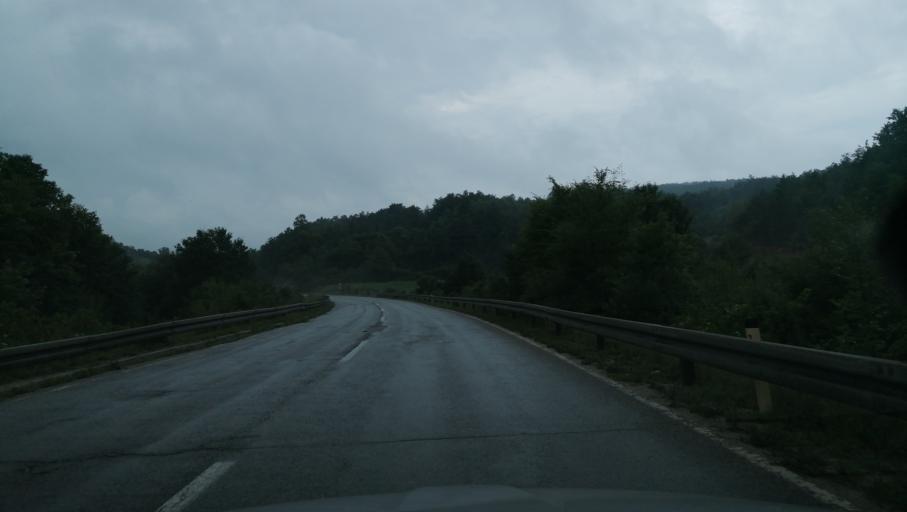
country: RS
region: Central Serbia
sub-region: Zlatiborski Okrug
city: Cajetina
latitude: 43.7887
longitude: 19.7189
